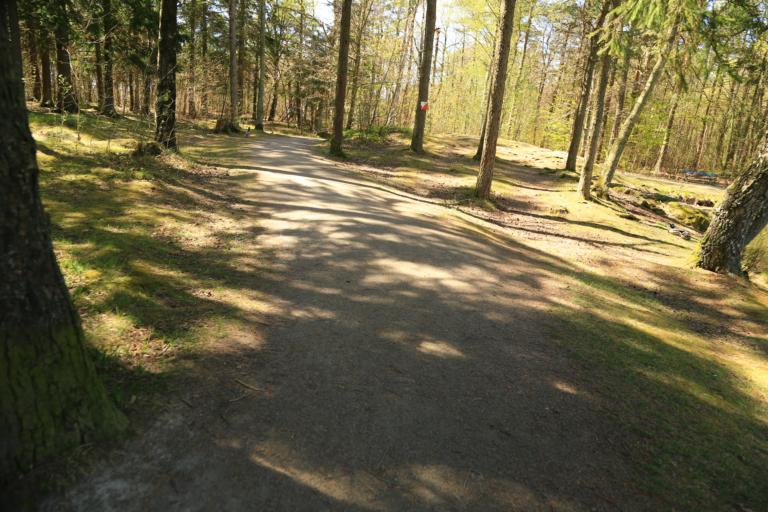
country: SE
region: Halland
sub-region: Varbergs Kommun
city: Varberg
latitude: 57.1168
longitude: 12.2684
